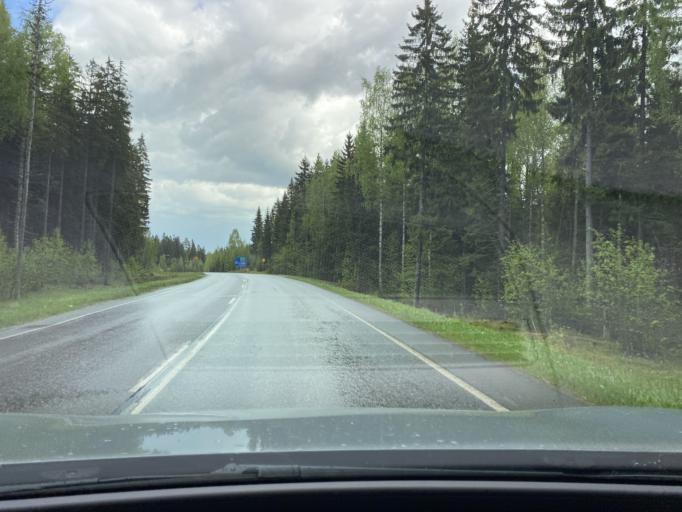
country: FI
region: Uusimaa
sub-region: Porvoo
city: Pukkila
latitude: 60.7740
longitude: 25.4432
